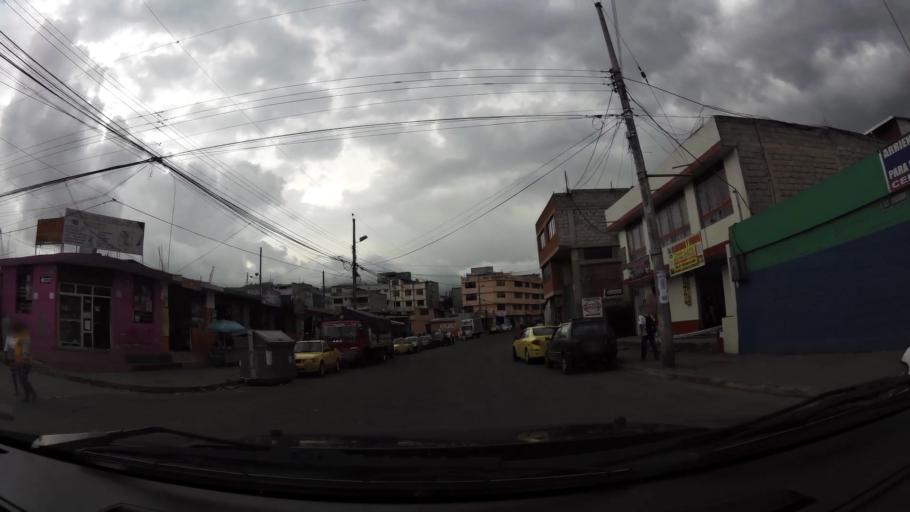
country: EC
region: Pichincha
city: Quito
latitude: -0.2748
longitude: -78.5363
